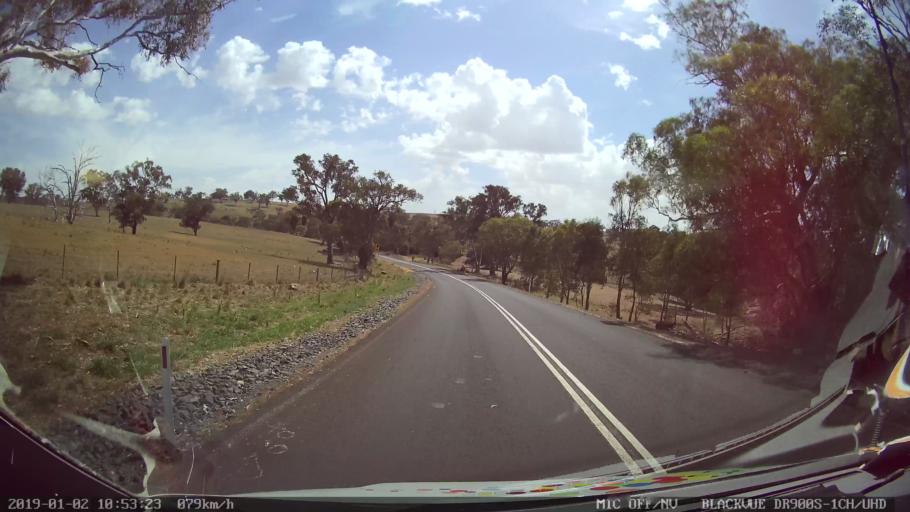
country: AU
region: New South Wales
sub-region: Cootamundra
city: Cootamundra
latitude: -34.6789
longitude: 148.2754
